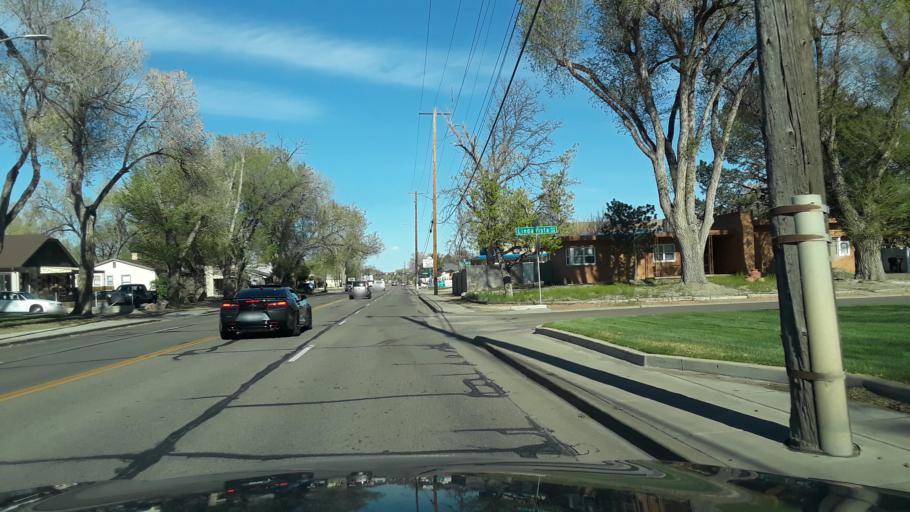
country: US
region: Colorado
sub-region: Pueblo County
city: Pueblo
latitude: 38.2585
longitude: -104.6483
